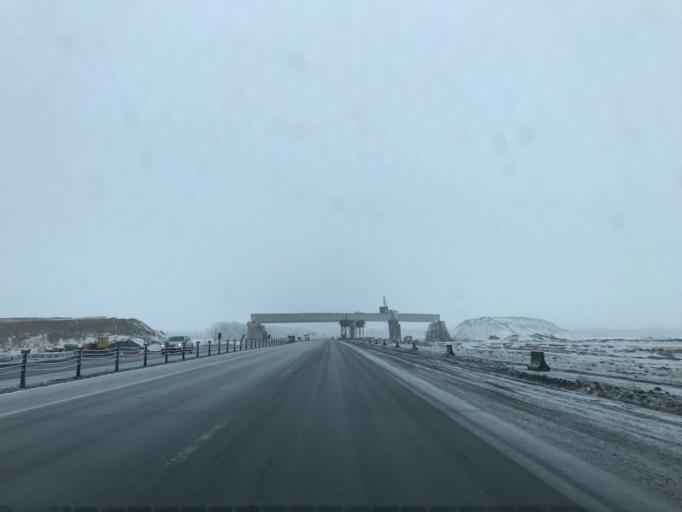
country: RU
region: Rostov
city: Grushevskaya
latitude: 47.5012
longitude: 39.9708
